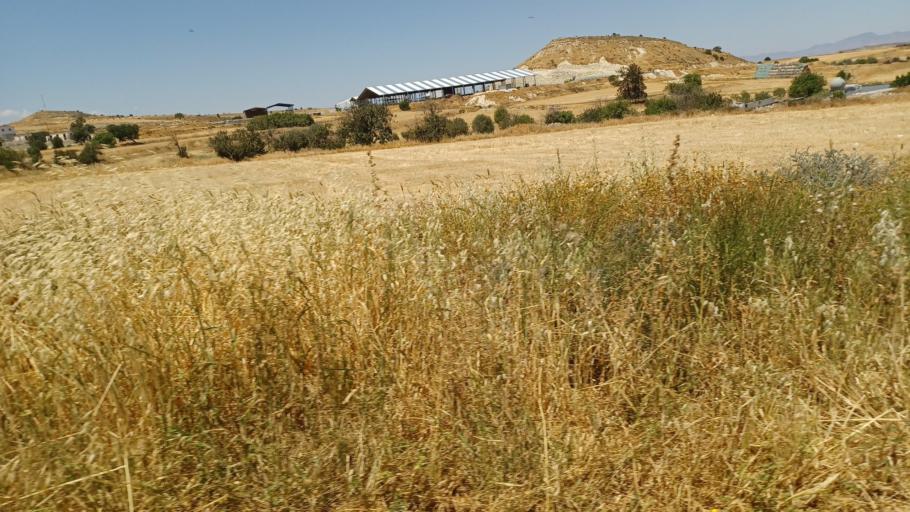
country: CY
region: Larnaka
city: Athienou
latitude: 35.0375
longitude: 33.5381
